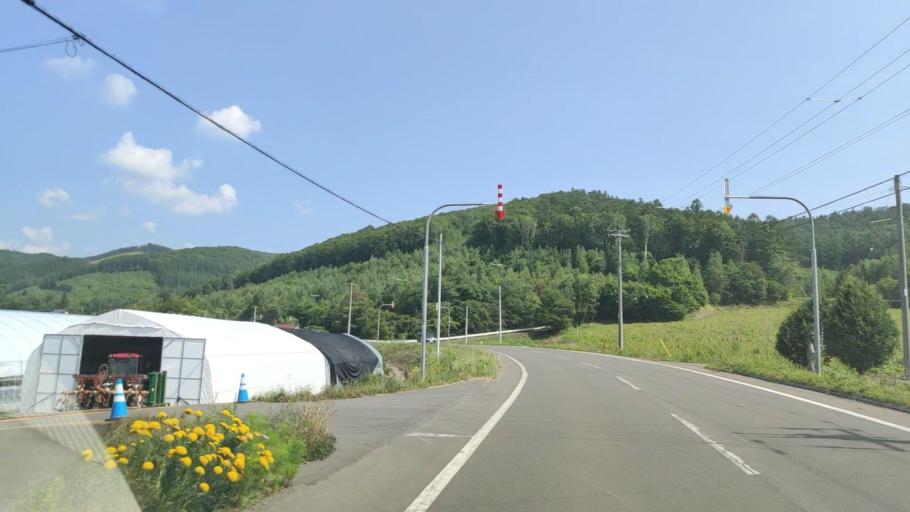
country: JP
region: Hokkaido
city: Shimo-furano
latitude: 43.4188
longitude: 142.4018
